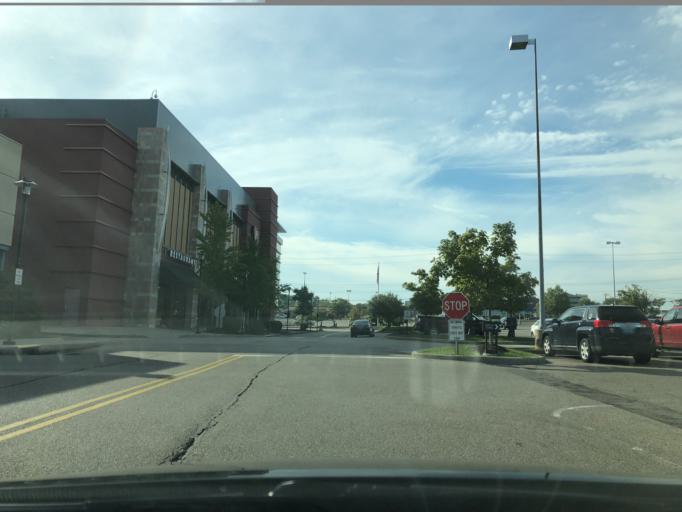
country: US
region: Ohio
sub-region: Hamilton County
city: Glendale
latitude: 39.2897
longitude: -84.4654
